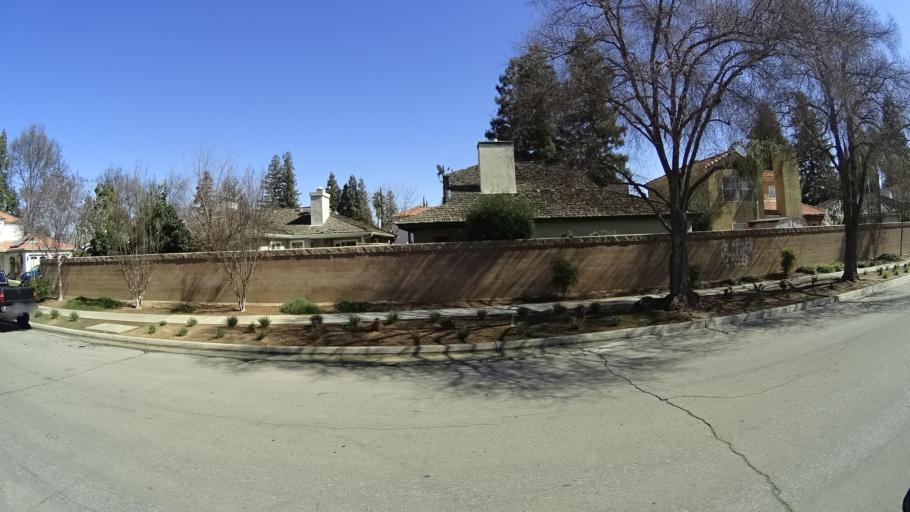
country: US
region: California
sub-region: Fresno County
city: Clovis
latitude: 36.8459
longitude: -119.7613
